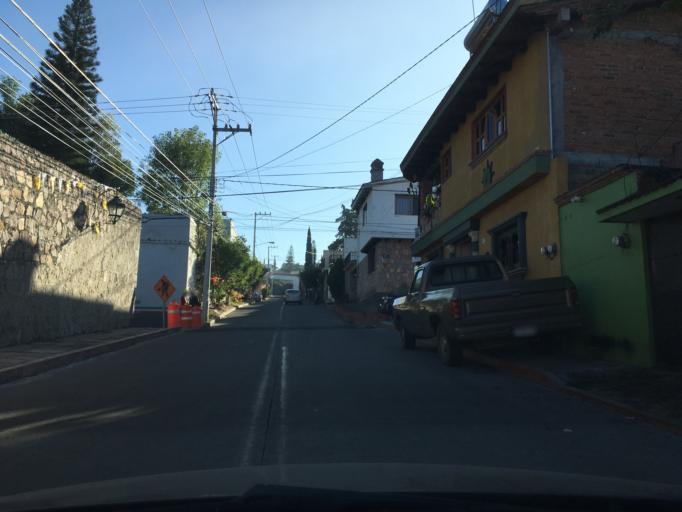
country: MX
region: Michoacan
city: Morelia
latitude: 19.6777
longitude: -101.1961
